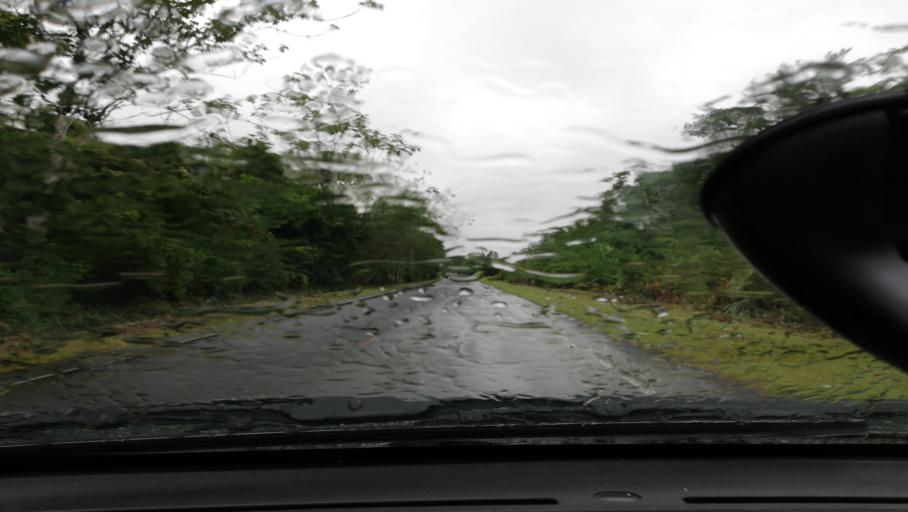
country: PE
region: Loreto
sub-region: Provincia de Maynas
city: San Juan
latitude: -4.0377
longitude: -73.4365
